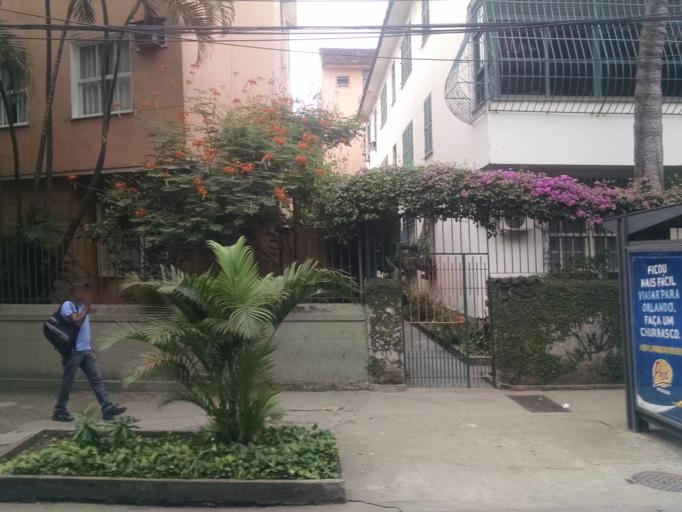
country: BR
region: Rio de Janeiro
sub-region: Rio De Janeiro
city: Rio de Janeiro
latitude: -22.9822
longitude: -43.2237
